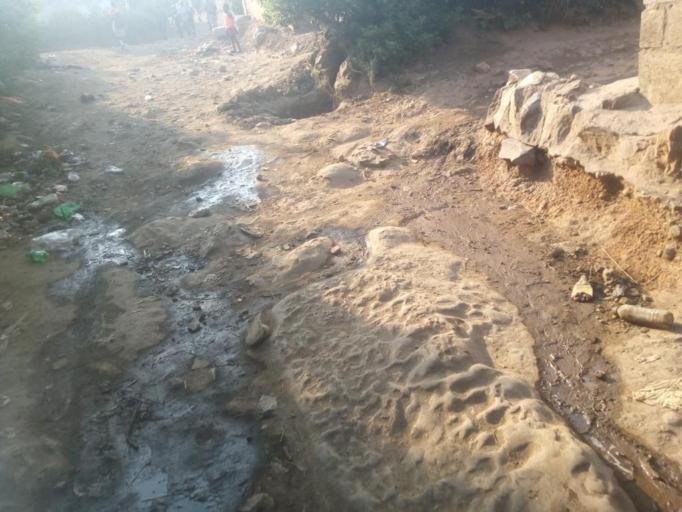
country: ZM
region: Lusaka
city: Lusaka
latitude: -15.4048
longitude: 28.3641
